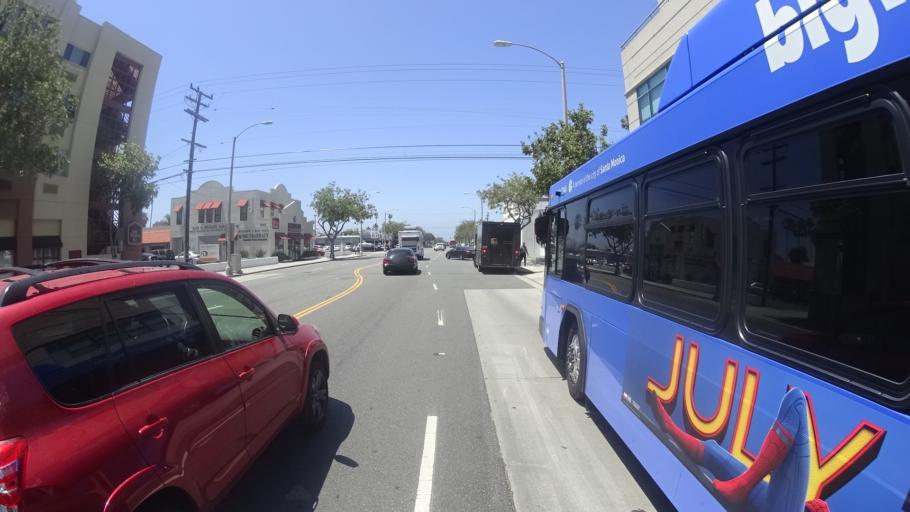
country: US
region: California
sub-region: Los Angeles County
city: Santa Monica
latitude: 34.0287
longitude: -118.4805
